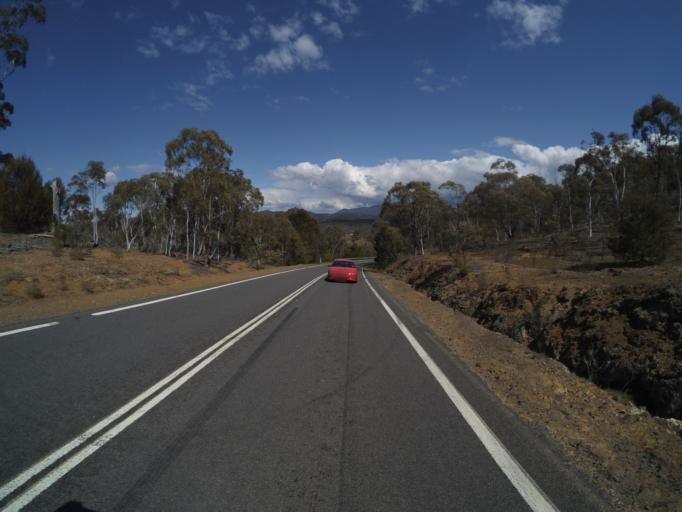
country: AU
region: Australian Capital Territory
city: Macquarie
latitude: -35.3161
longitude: 148.9488
